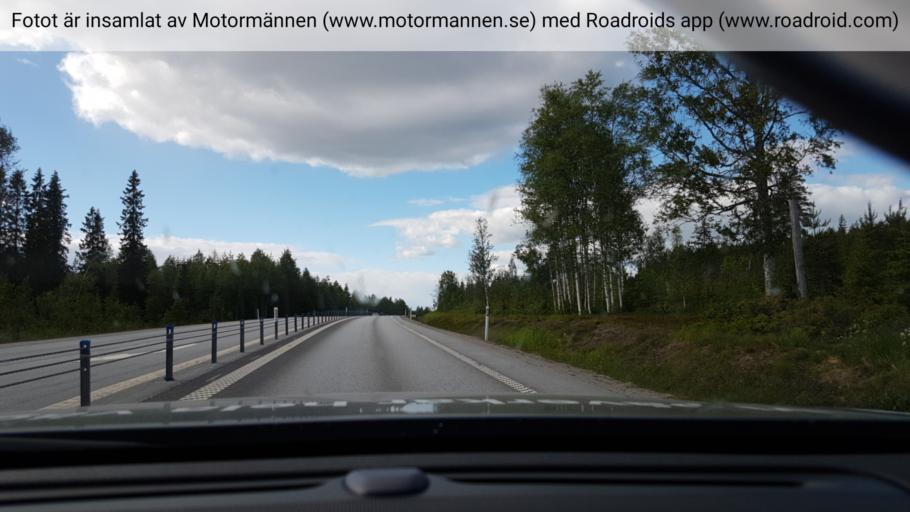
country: SE
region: Vaesterbotten
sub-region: Vannas Kommun
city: Vannasby
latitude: 63.9036
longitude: 19.8947
